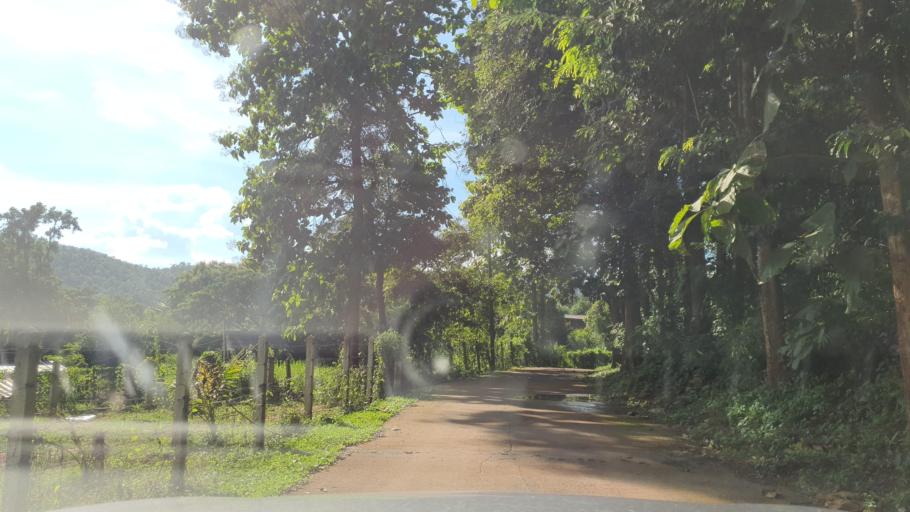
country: TH
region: Chiang Mai
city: Mae On
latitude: 18.7363
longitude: 99.3067
